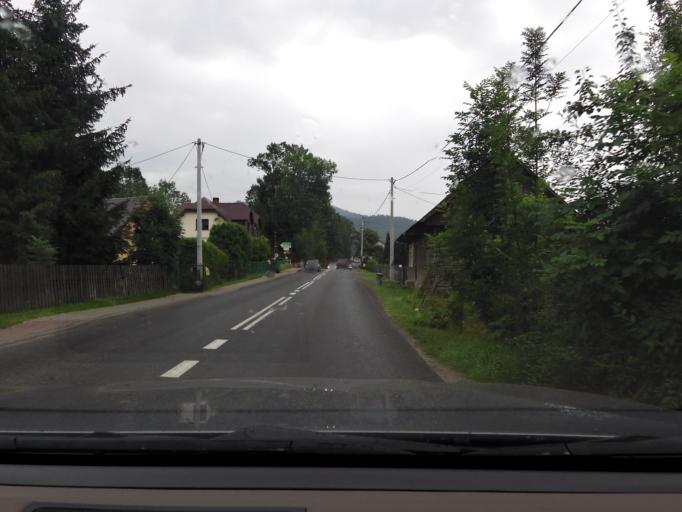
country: PL
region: Silesian Voivodeship
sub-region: Powiat zywiecki
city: Milowka
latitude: 49.5499
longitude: 19.0954
